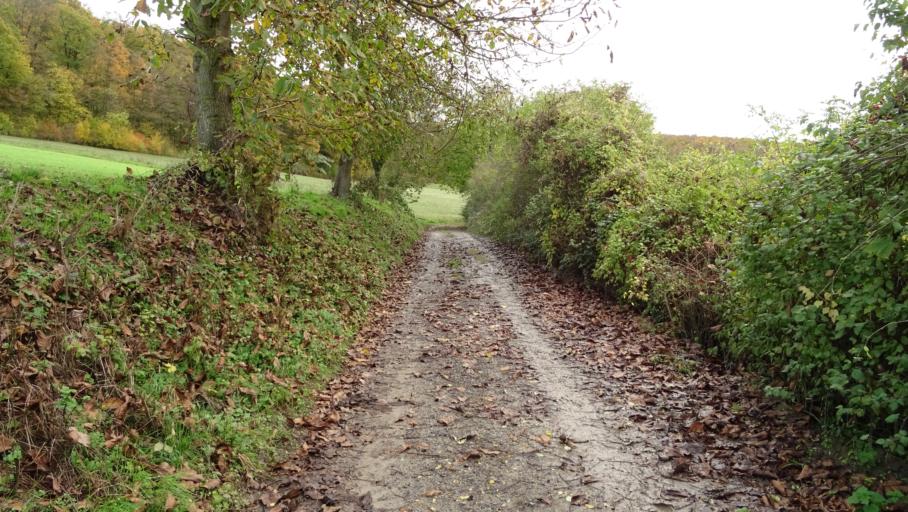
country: DE
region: Baden-Wuerttemberg
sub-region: Karlsruhe Region
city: Obrigheim
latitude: 49.3761
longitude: 9.0899
